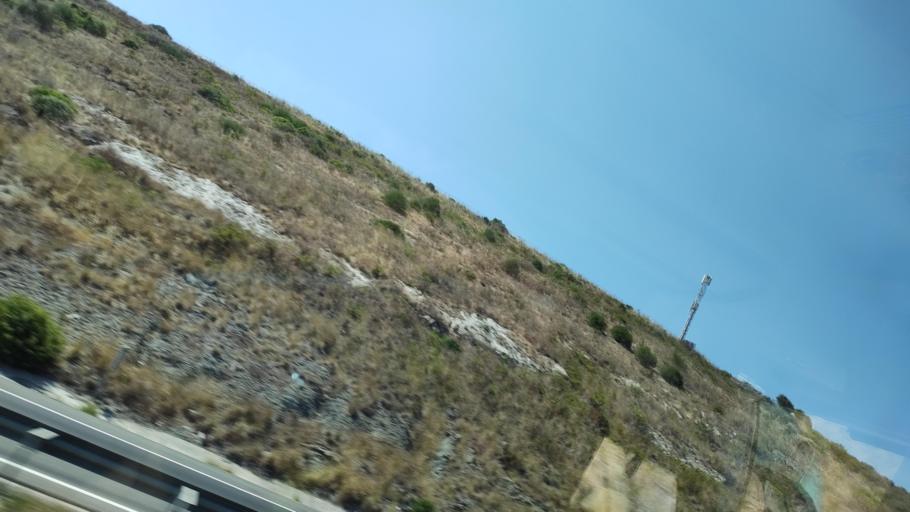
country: ES
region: Andalusia
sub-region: Provincia de Malaga
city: Manilva
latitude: 36.3245
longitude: -5.2654
